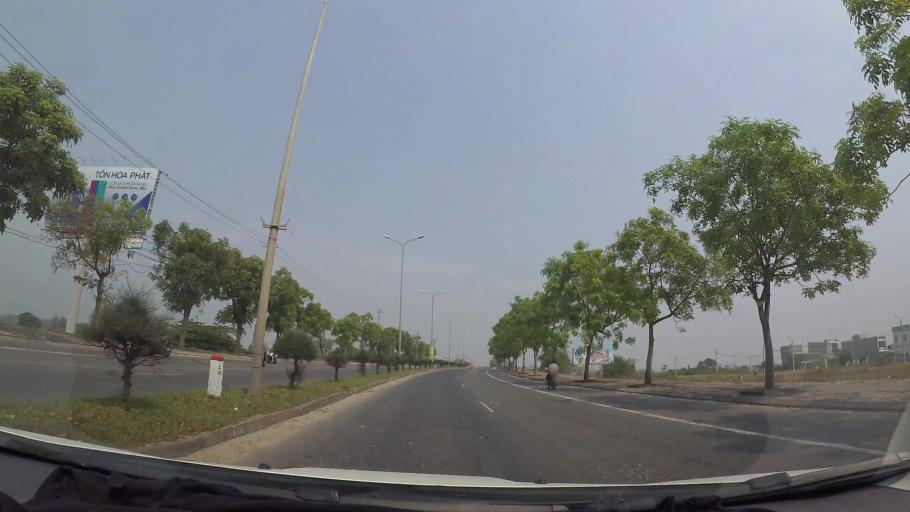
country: VN
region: Da Nang
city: Cam Le
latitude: 15.9705
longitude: 108.2093
